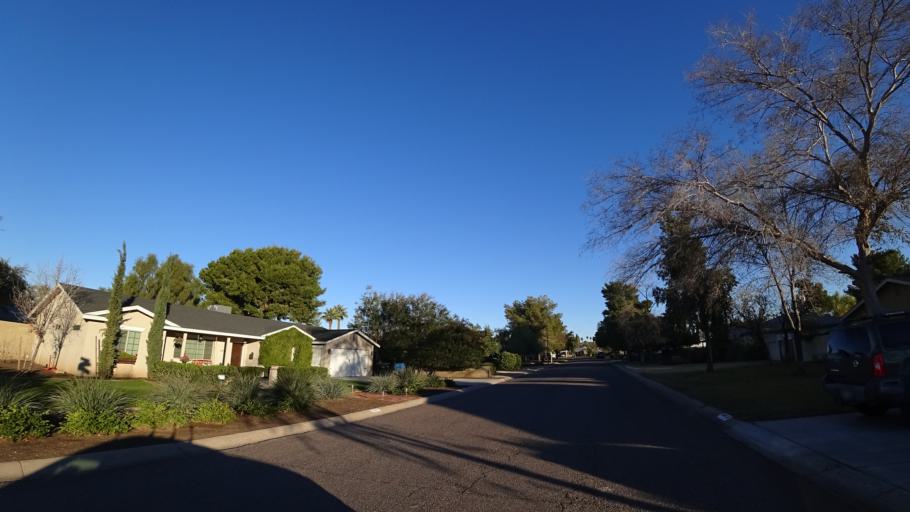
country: US
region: Arizona
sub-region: Maricopa County
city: Paradise Valley
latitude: 33.4916
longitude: -112.0051
